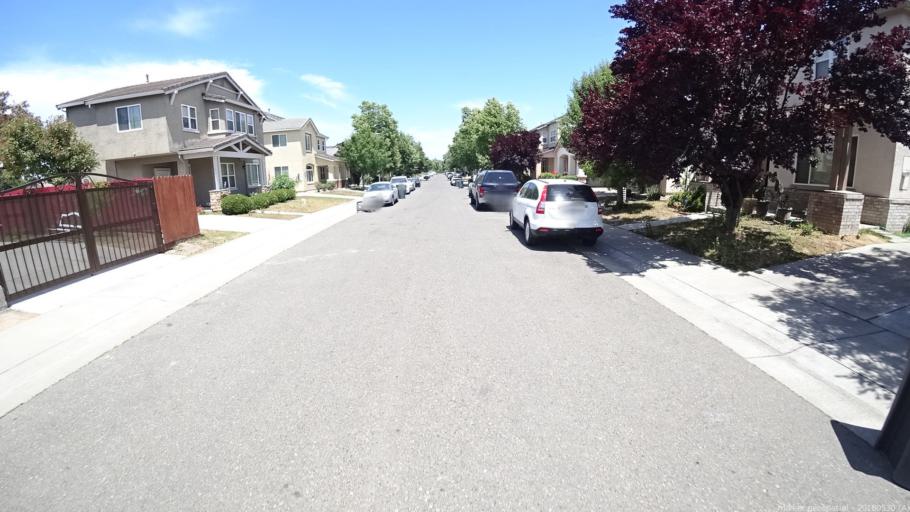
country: US
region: California
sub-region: Sacramento County
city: Sacramento
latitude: 38.6273
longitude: -121.4537
